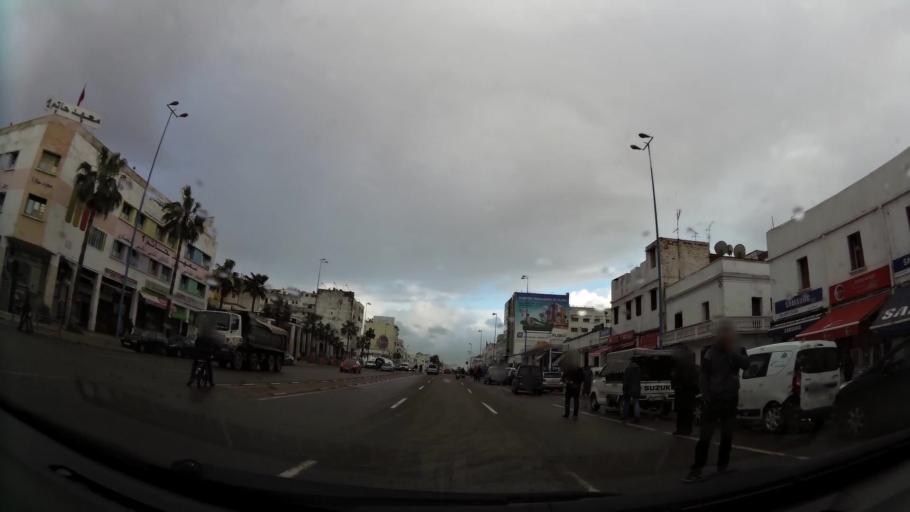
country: MA
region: Grand Casablanca
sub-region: Casablanca
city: Casablanca
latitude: 33.5781
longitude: -7.6003
